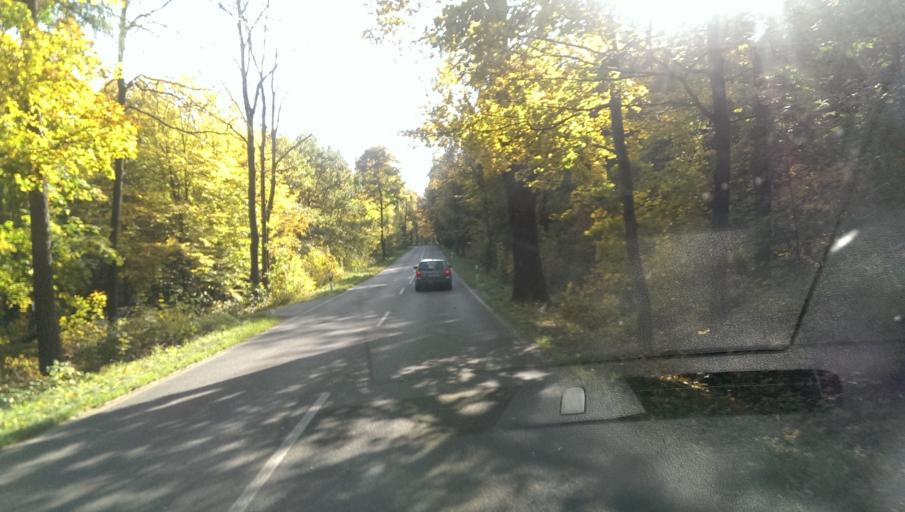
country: DE
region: Saxony
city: Dohma
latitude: 50.8516
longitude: 13.9579
